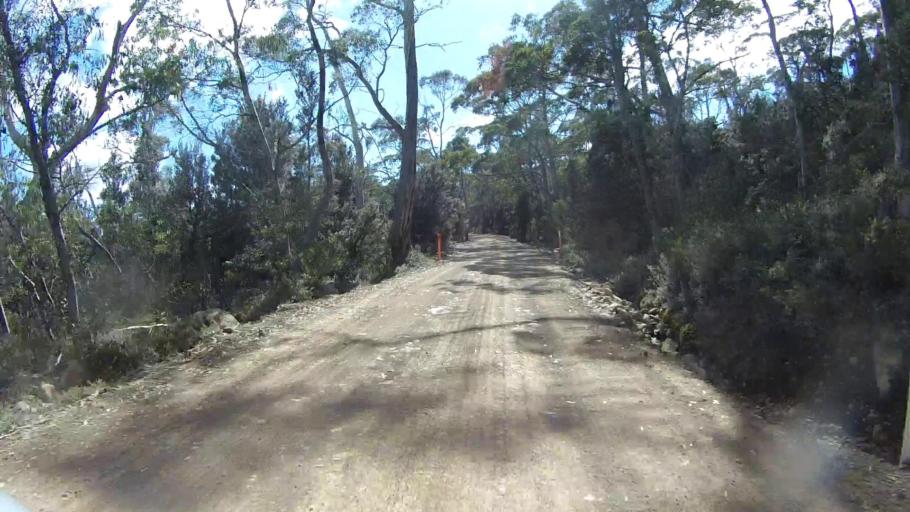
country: AU
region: Tasmania
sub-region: Derwent Valley
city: New Norfolk
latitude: -42.6863
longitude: 146.6041
